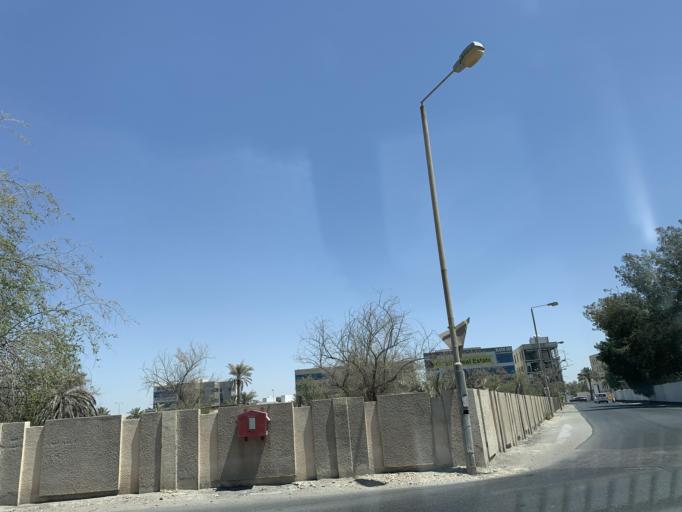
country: BH
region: Manama
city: Jidd Hafs
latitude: 26.2206
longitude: 50.4900
